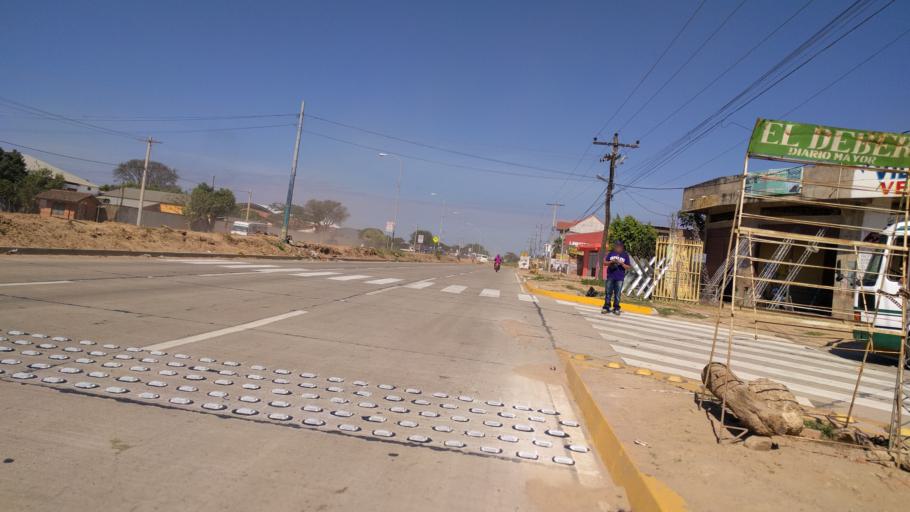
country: BO
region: Santa Cruz
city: Santa Cruz de la Sierra
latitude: -17.8524
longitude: -63.1840
